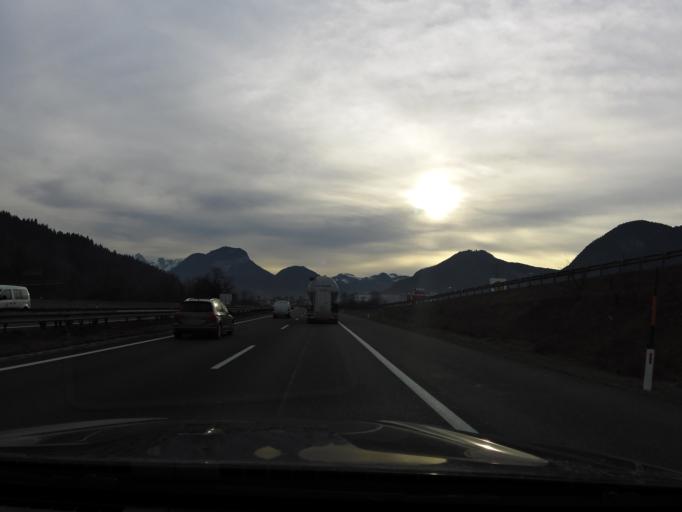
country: AT
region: Tyrol
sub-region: Politischer Bezirk Kufstein
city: Worgl
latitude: 47.4837
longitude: 12.0273
